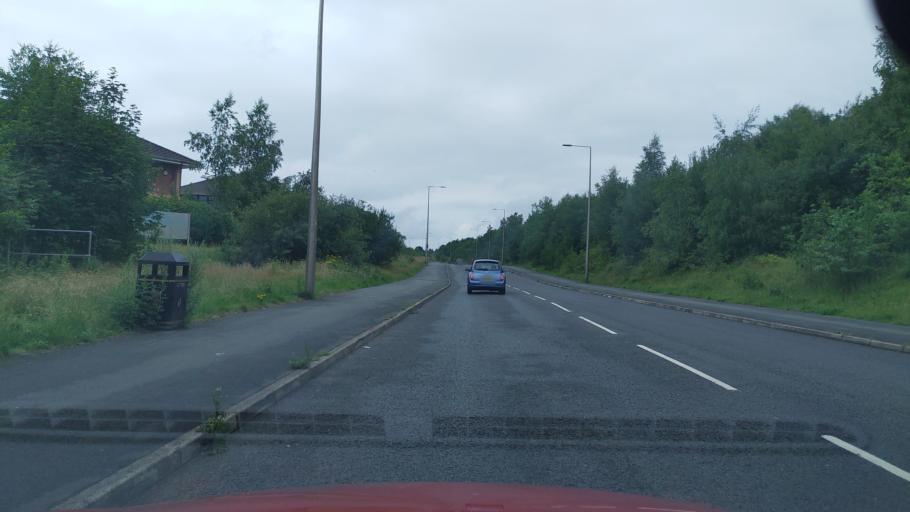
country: GB
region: England
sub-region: Borough of Wigan
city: Ince-in-Makerfield
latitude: 53.5290
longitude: -2.6563
